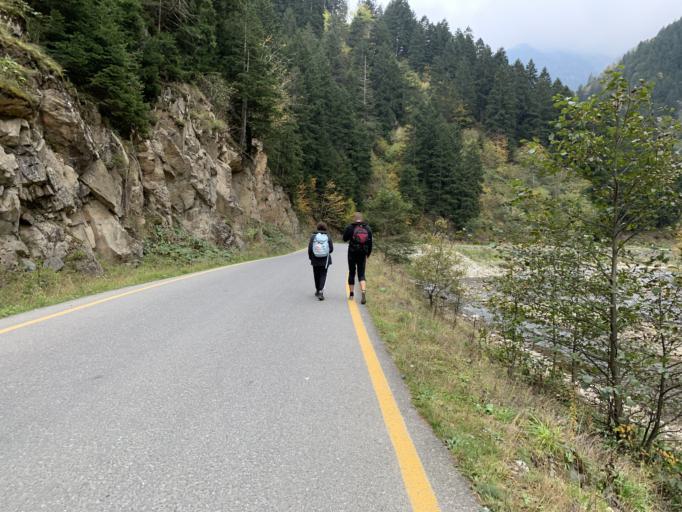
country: TR
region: Trabzon
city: Uzungol
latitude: 40.6031
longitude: 40.3172
